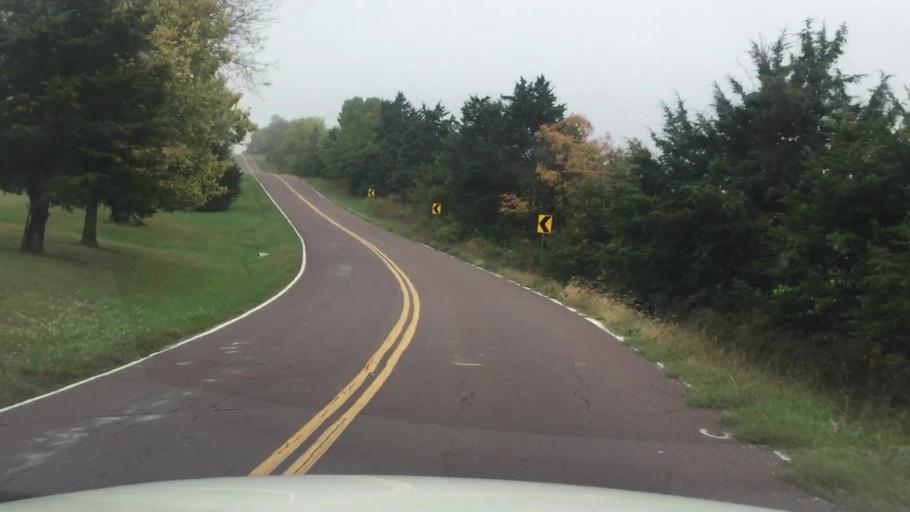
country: US
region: Missouri
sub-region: Boone County
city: Columbia
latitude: 38.8469
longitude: -92.3370
